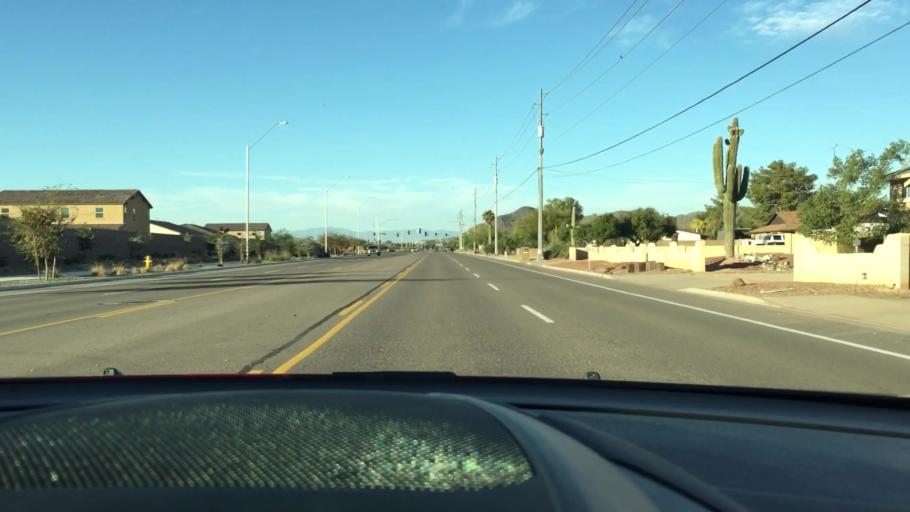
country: US
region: Arizona
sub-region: Maricopa County
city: Sun City West
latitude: 33.6862
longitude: -112.2550
